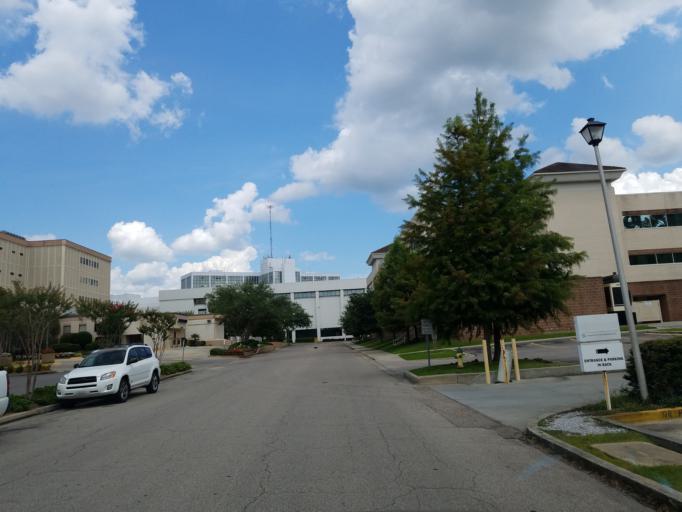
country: US
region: Mississippi
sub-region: Lamar County
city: West Hattiesburg
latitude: 31.3184
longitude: -89.3329
